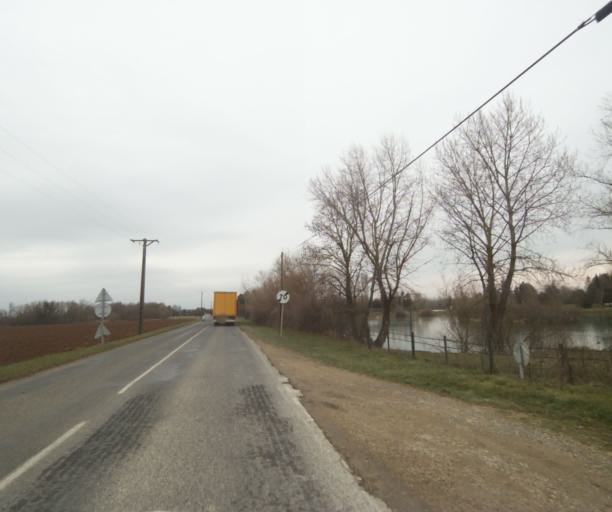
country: FR
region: Champagne-Ardenne
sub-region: Departement de la Haute-Marne
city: Villiers-en-Lieu
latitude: 48.6467
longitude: 4.9061
